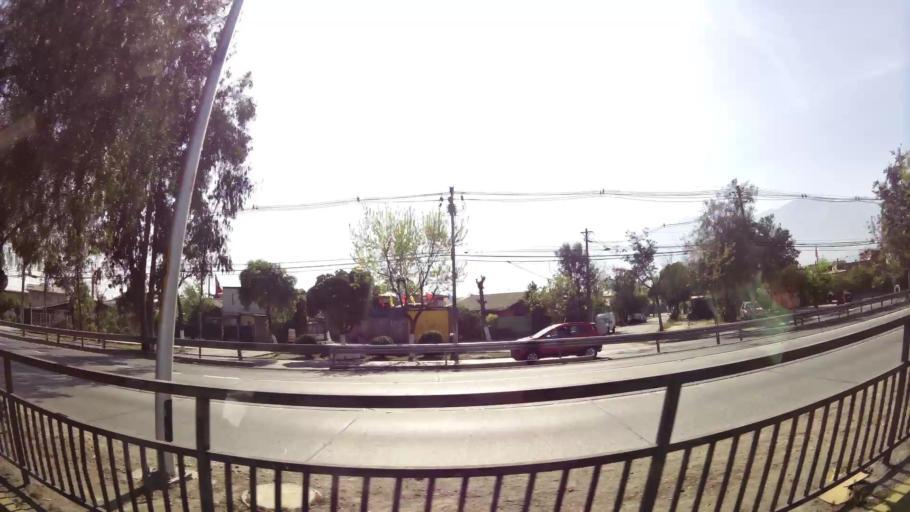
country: CL
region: Santiago Metropolitan
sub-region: Provincia de Santiago
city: Villa Presidente Frei, Nunoa, Santiago, Chile
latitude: -33.5203
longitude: -70.5800
